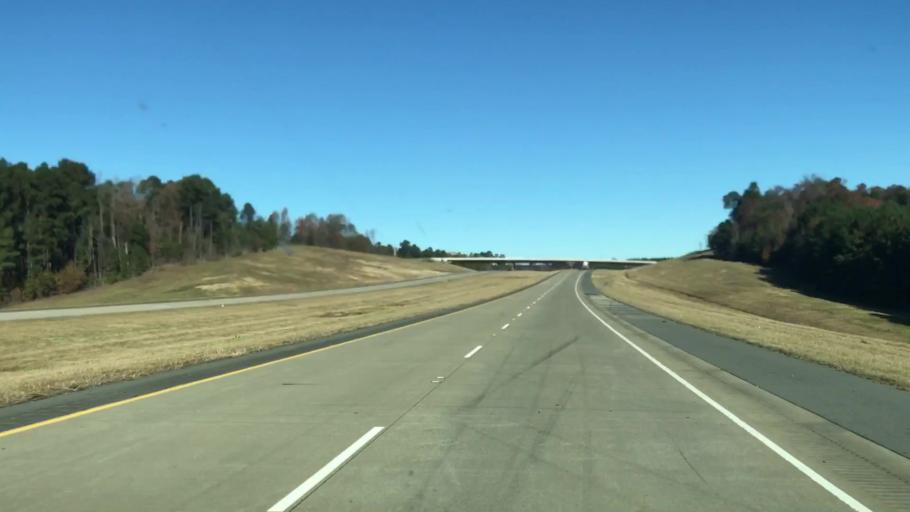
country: US
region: Louisiana
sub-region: Caddo Parish
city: Vivian
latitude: 32.9735
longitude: -93.9081
